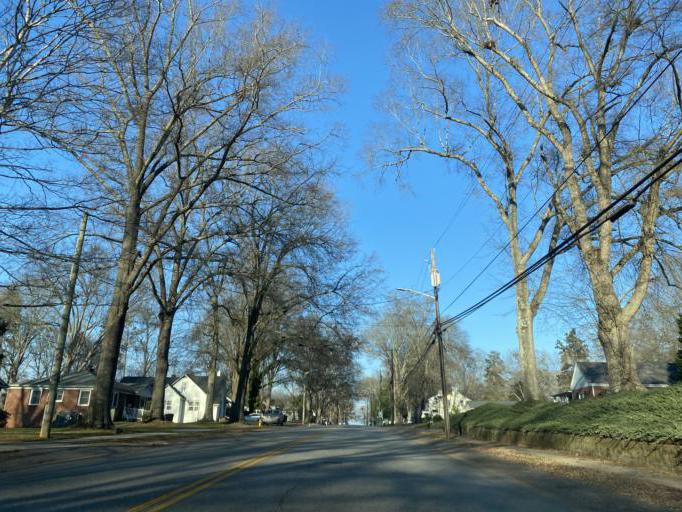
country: US
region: South Carolina
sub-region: Cherokee County
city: Gaffney
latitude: 35.0665
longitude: -81.6549
